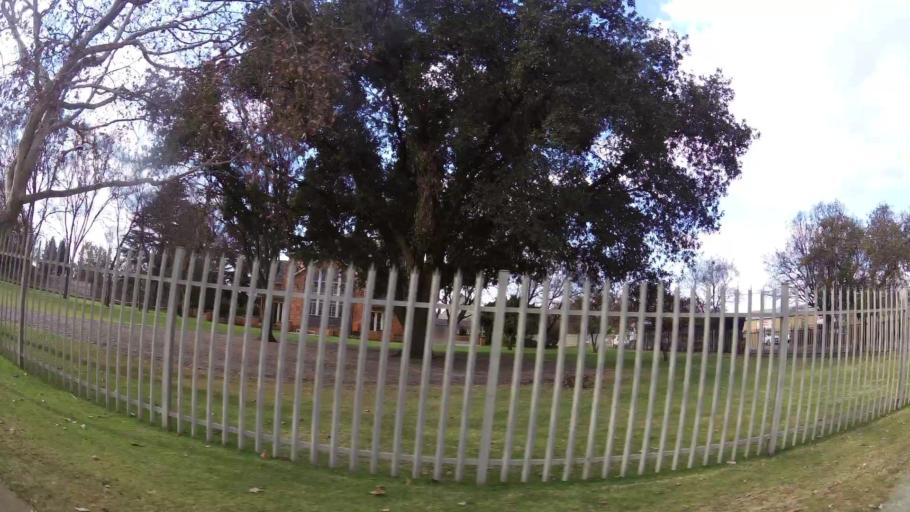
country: ZA
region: Mpumalanga
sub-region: Nkangala District Municipality
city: Delmas
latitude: -26.1478
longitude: 28.6846
